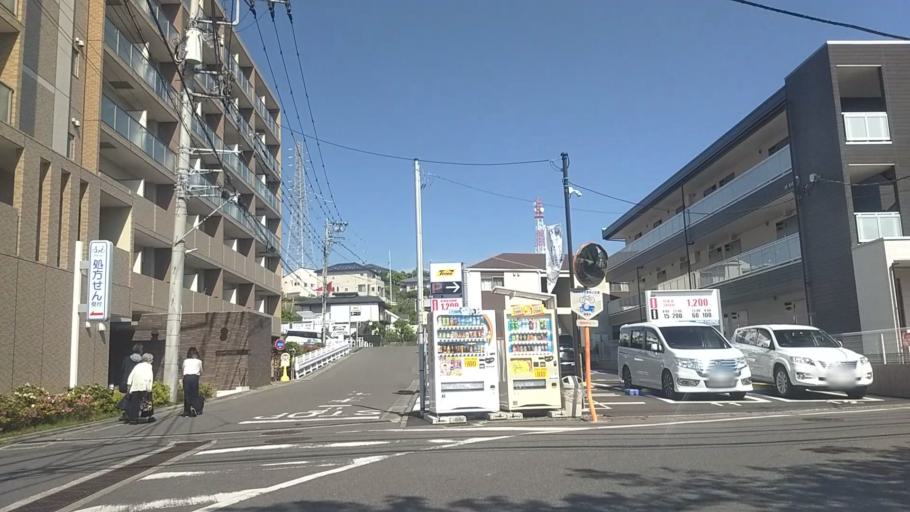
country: JP
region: Kanagawa
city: Kamakura
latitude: 35.3513
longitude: 139.5390
